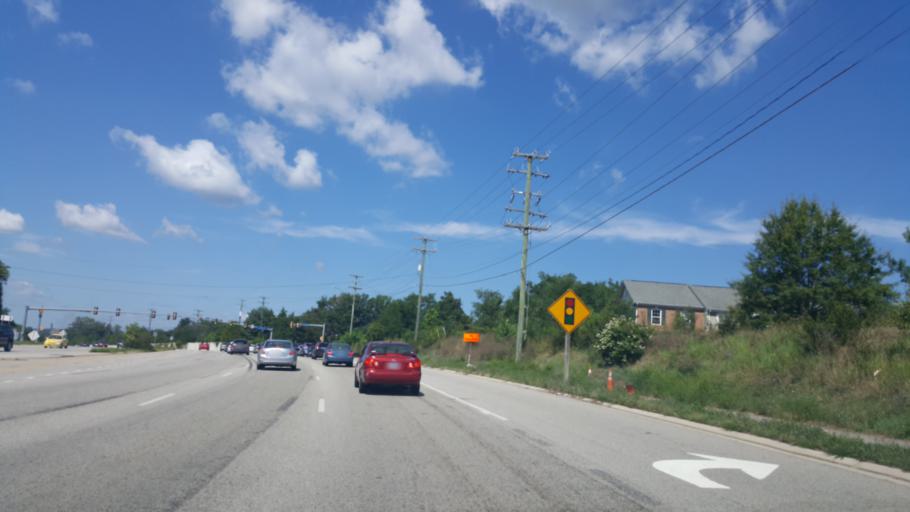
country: US
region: Virginia
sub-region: Fairfax County
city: Newington
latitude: 38.7100
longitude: -77.1953
